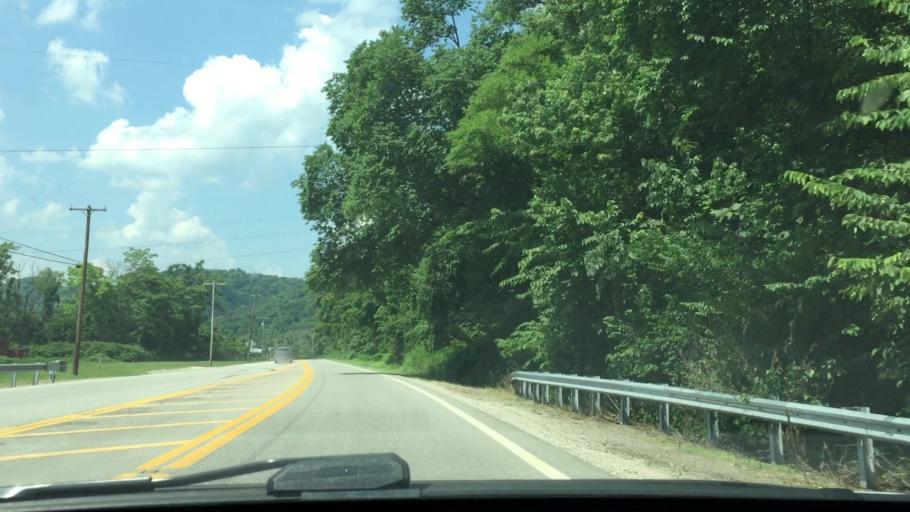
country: US
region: West Virginia
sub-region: Wetzel County
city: New Martinsville
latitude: 39.7142
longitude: -80.8221
